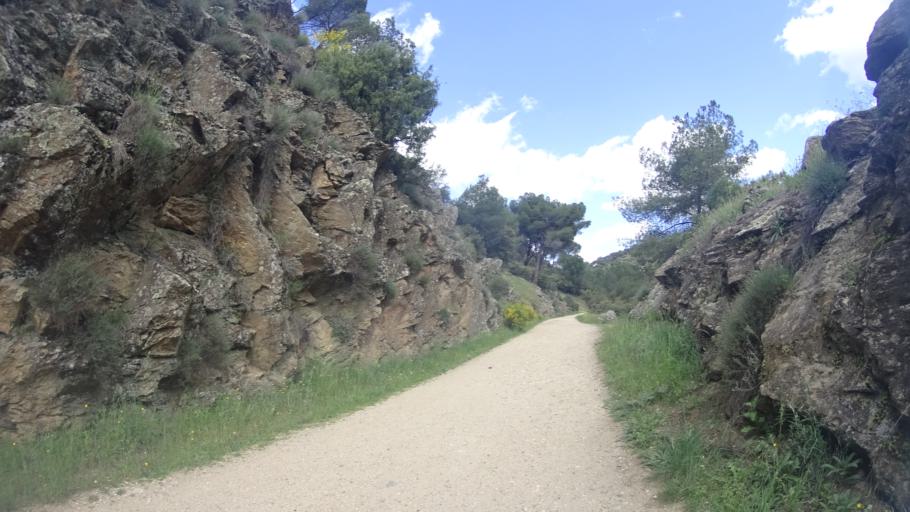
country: ES
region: Madrid
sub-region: Provincia de Madrid
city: Pelayos de la Presa
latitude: 40.3632
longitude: -4.2976
